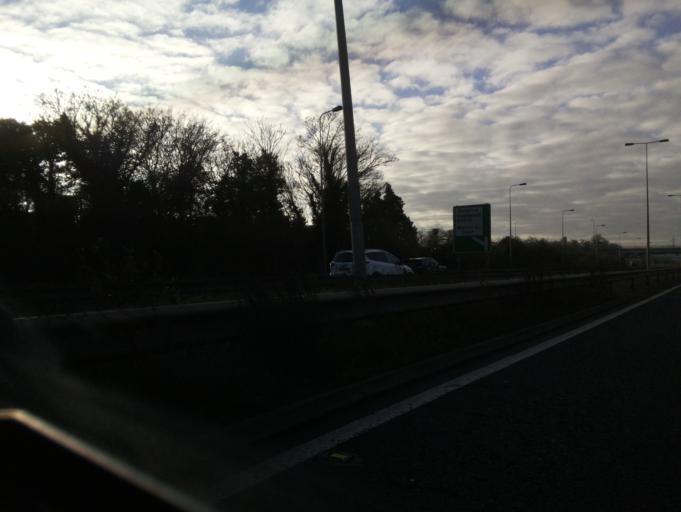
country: GB
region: England
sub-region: Staffordshire
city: Barton under Needwood
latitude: 52.7637
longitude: -1.6982
